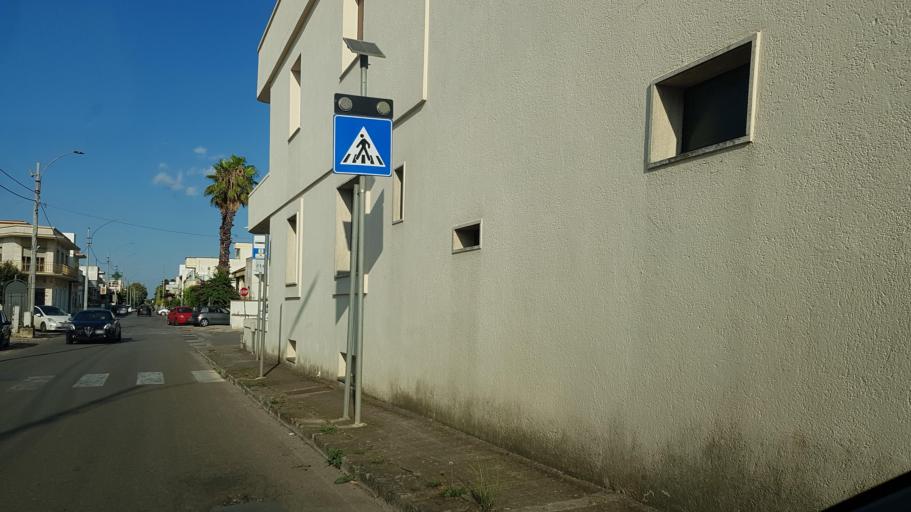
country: IT
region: Apulia
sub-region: Provincia di Lecce
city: Miggiano
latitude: 39.9654
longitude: 18.3113
